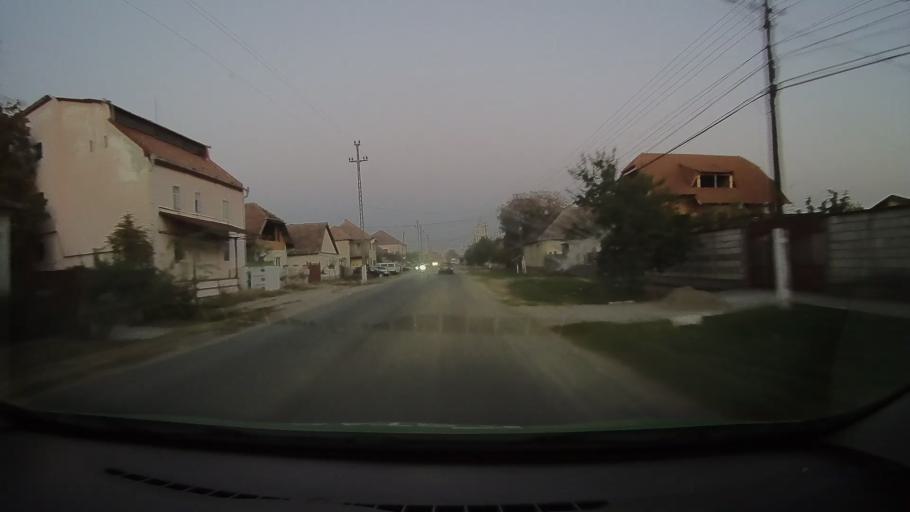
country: RO
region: Arad
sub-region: Comuna Livada
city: Livada
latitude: 46.2258
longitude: 21.3827
